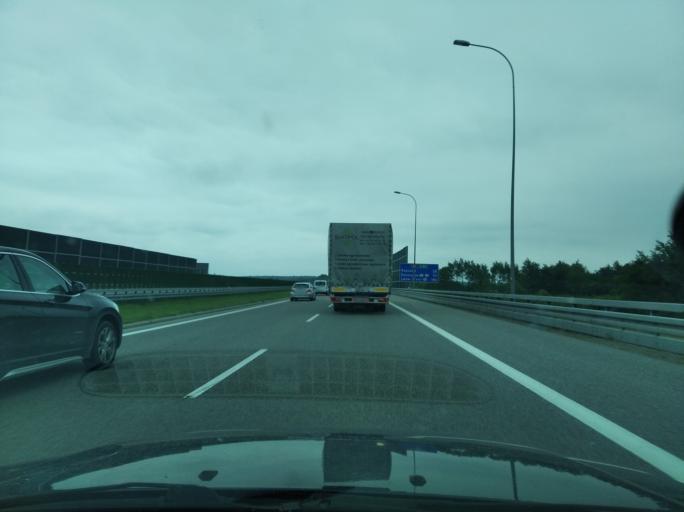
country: PL
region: Subcarpathian Voivodeship
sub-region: Powiat ropczycko-sedziszowski
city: Sedziszow Malopolski
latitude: 50.1073
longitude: 21.6725
